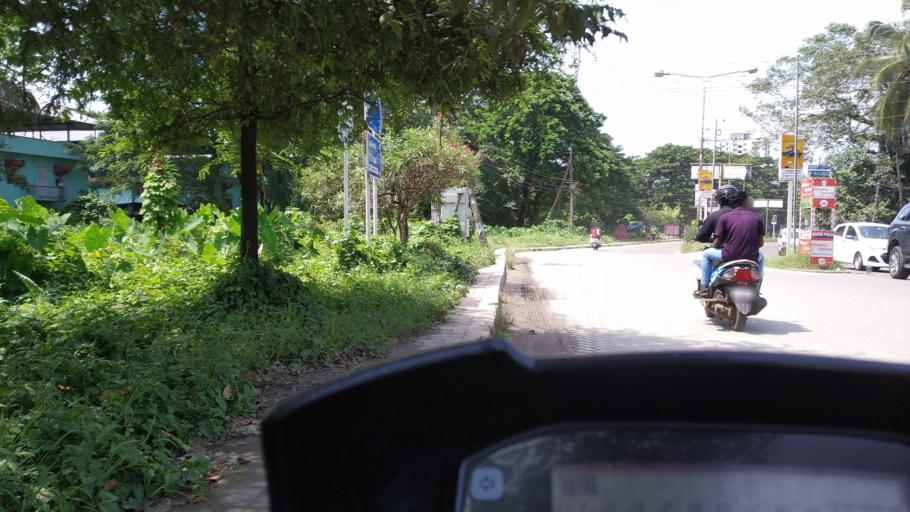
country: IN
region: Kerala
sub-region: Ernakulam
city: Cochin
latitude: 9.9707
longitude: 76.2985
